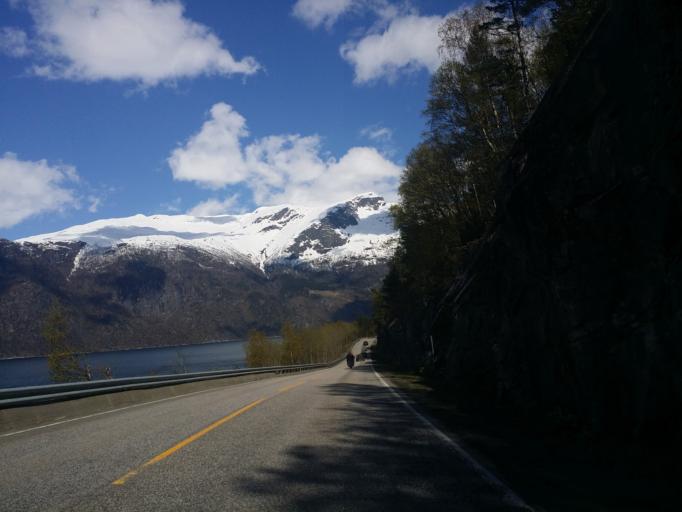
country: NO
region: Hordaland
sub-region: Ulvik
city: Ulvik
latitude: 60.4763
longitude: 6.9587
